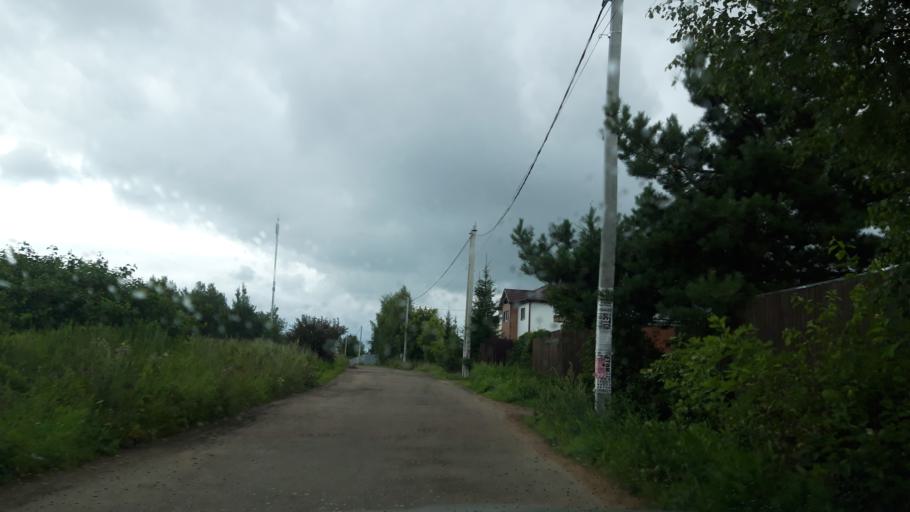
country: RU
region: Moskovskaya
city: Povarovo
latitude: 56.0958
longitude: 37.0705
